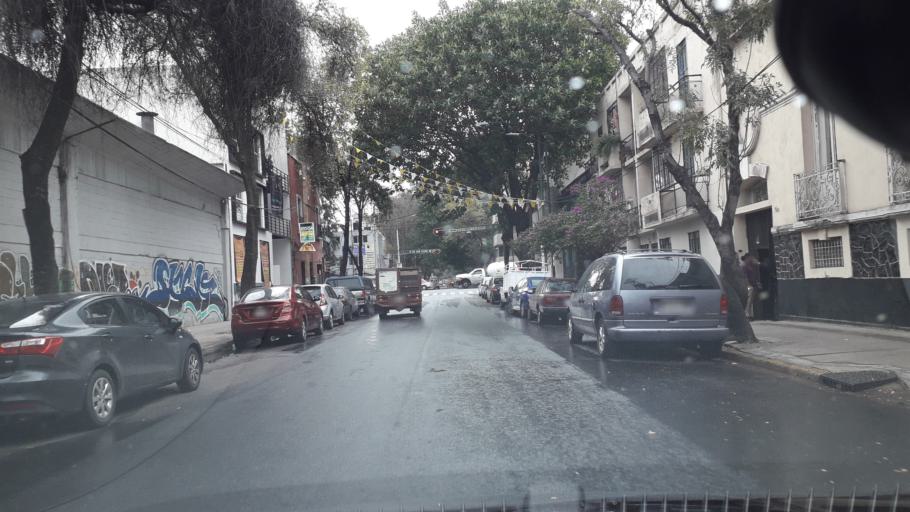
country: MX
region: Mexico City
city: Cuauhtemoc
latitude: 19.4476
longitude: -99.1566
